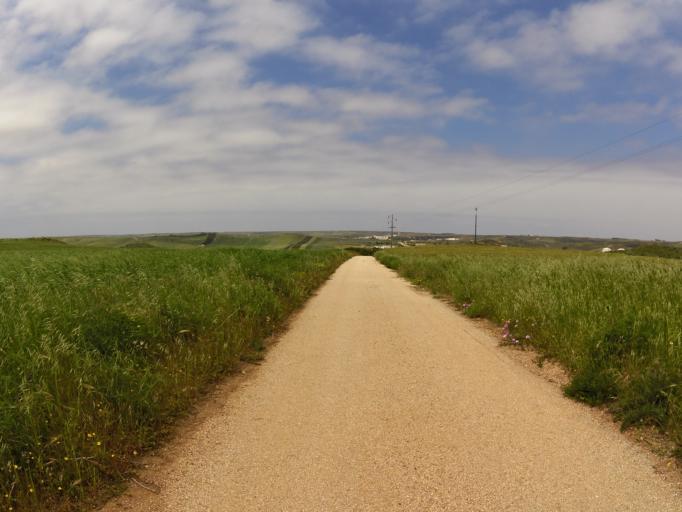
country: PT
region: Faro
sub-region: Vila do Bispo
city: Vila do Bispo
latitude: 37.0798
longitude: -8.8804
